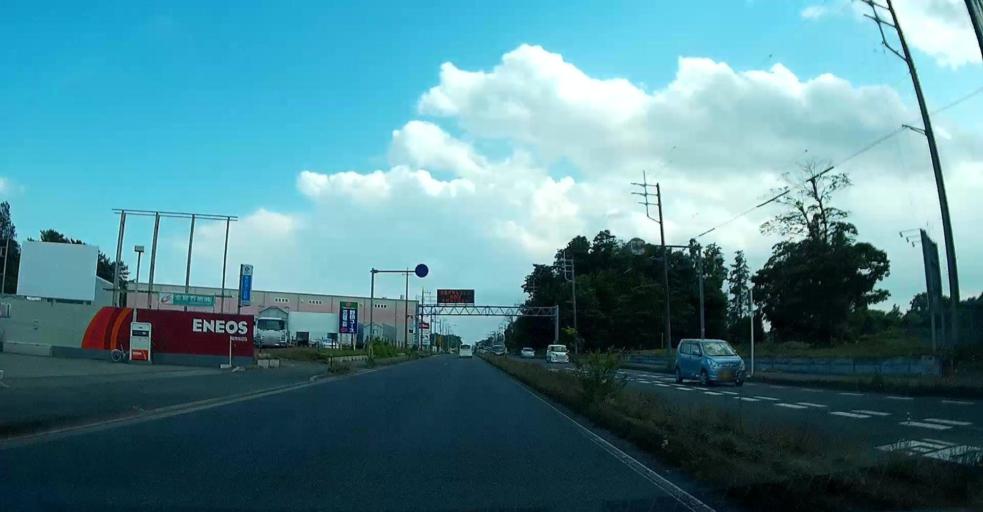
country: JP
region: Chiba
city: Noda
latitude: 35.9739
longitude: 139.8647
